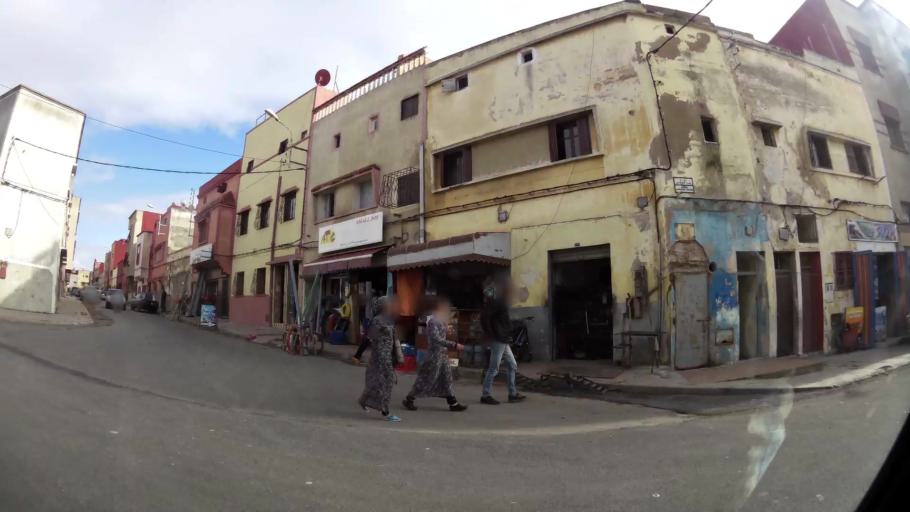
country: MA
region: Doukkala-Abda
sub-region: El-Jadida
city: El Jadida
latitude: 33.2536
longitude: -8.5170
